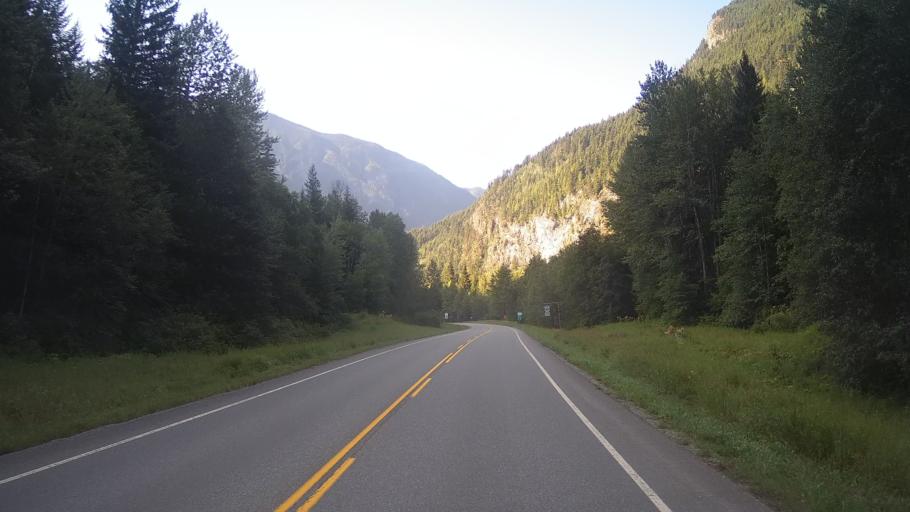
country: CA
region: British Columbia
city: Lillooet
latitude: 50.5888
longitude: -122.0938
